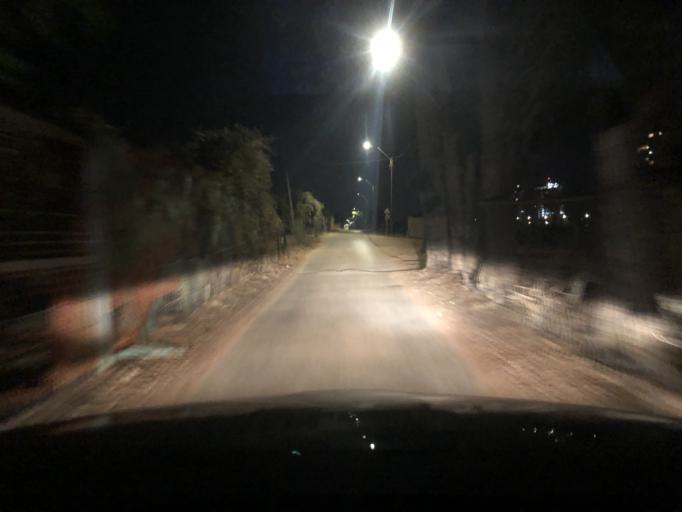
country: IL
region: Central District
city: Hod HaSharon
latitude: 32.1631
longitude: 34.8963
